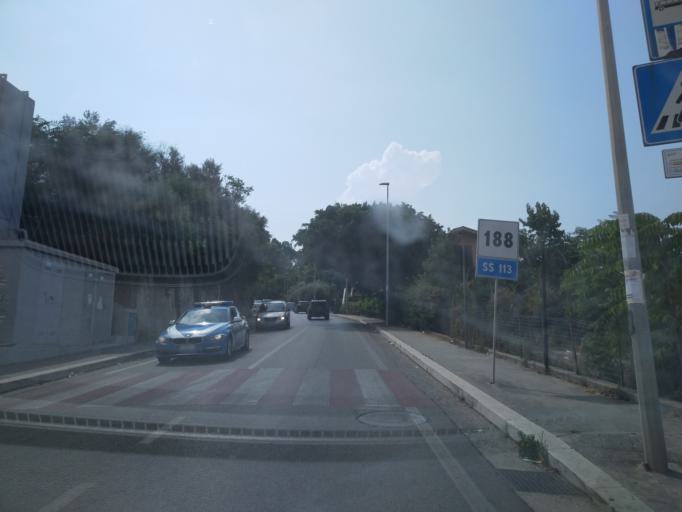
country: IT
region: Sicily
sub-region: Palermo
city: Cefalu
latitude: 38.0314
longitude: 14.0086
